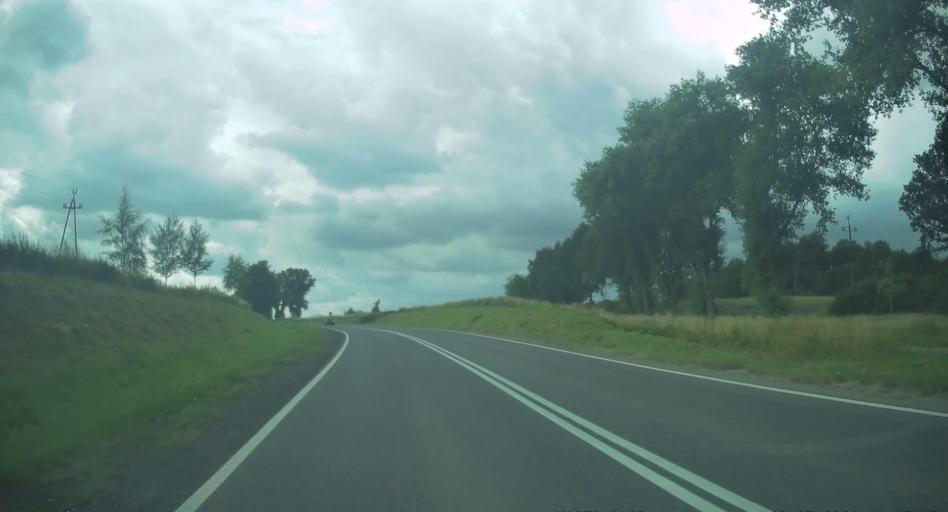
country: PL
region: Opole Voivodeship
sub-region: Powiat prudnicki
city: Laka Prudnicka
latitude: 50.4009
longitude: 17.5084
